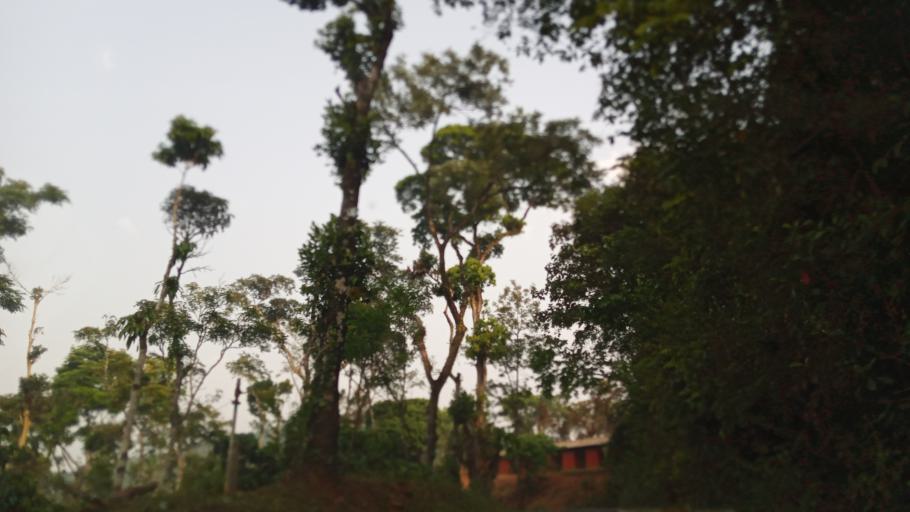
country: IN
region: Karnataka
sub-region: Chikmagalur
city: Mudigere
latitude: 13.0149
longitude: 75.6276
